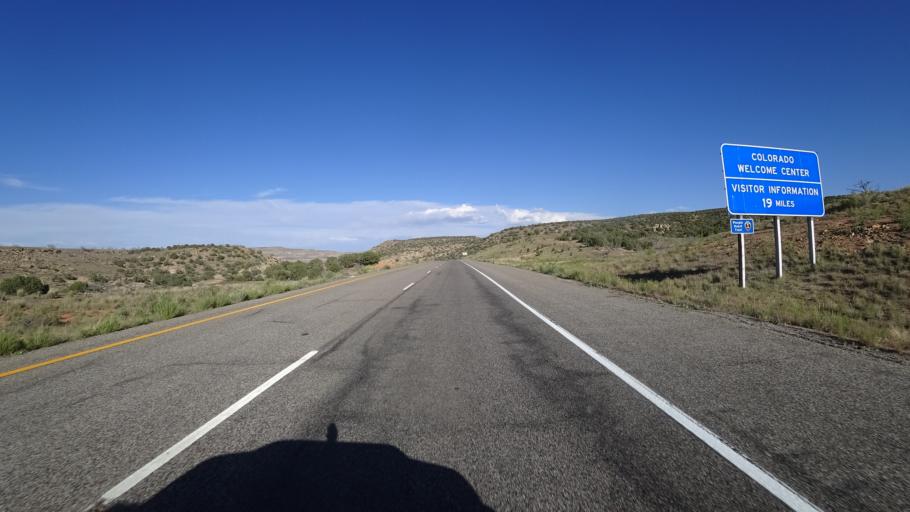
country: US
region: Colorado
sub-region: Mesa County
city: Loma
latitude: 39.1889
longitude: -109.0400
